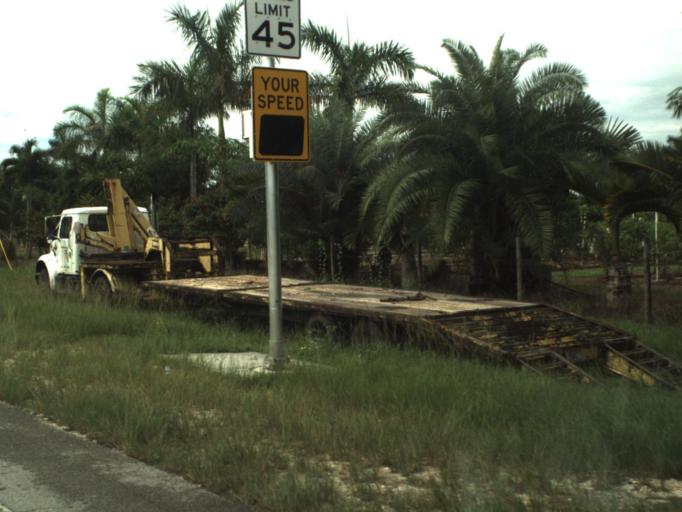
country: US
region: Florida
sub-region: Miami-Dade County
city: Naranja
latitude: 25.5472
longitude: -80.4781
